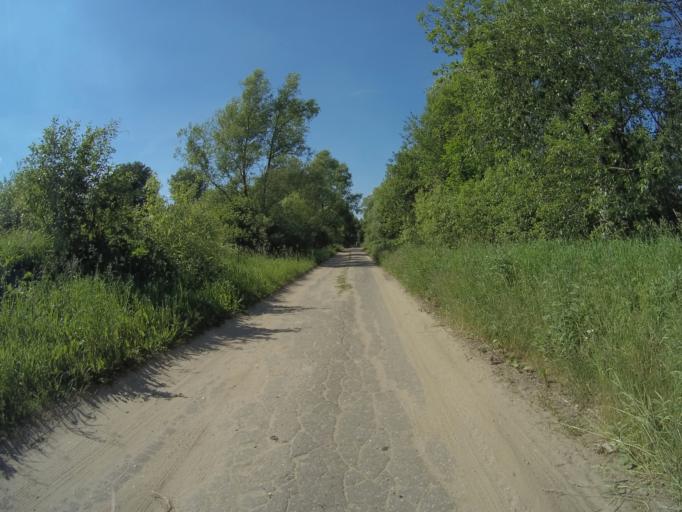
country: RU
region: Vladimir
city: Raduzhnyy
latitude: 56.0028
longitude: 40.3692
